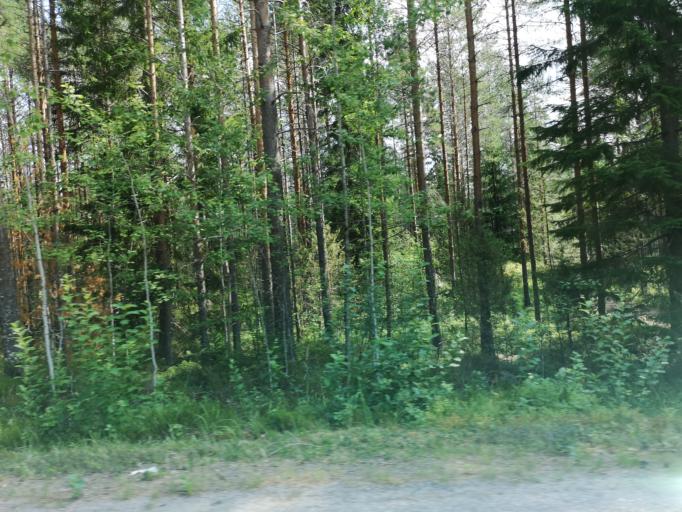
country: FI
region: Varsinais-Suomi
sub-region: Salo
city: Suomusjaervi
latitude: 60.3349
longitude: 23.6493
